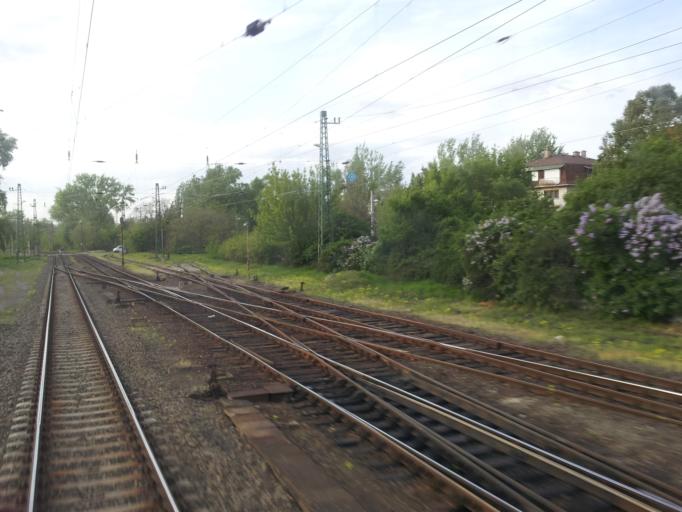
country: HU
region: Budapest
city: Budapest XVI. keruelet
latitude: 47.5241
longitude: 19.1441
